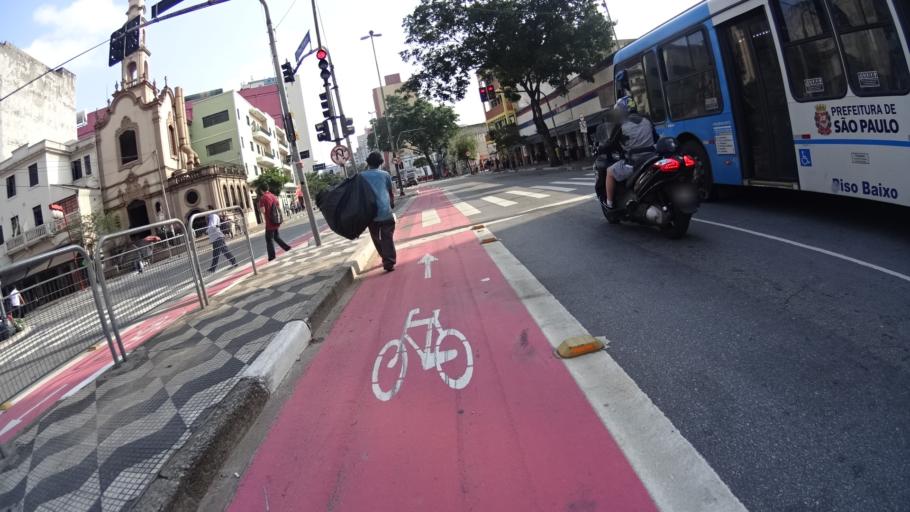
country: BR
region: Sao Paulo
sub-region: Sao Paulo
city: Sao Paulo
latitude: -23.5553
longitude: -46.6358
